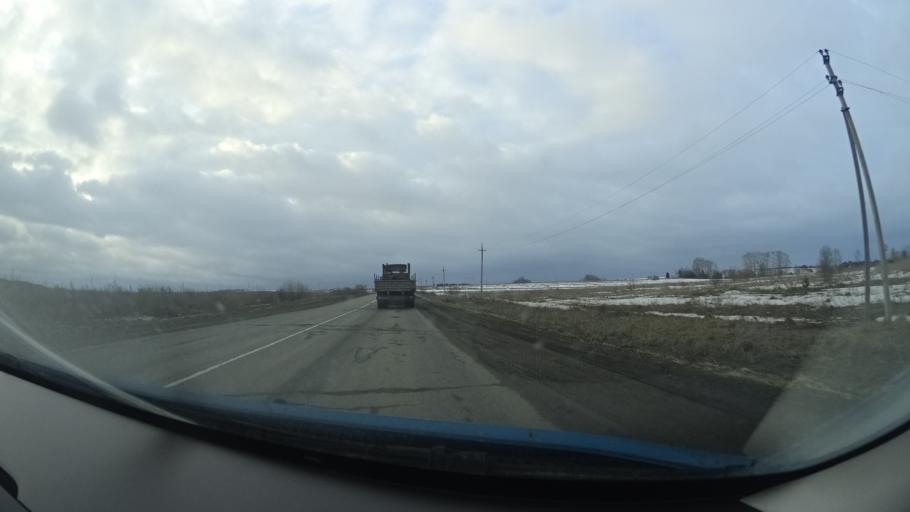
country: RU
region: Perm
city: Osa
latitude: 57.2543
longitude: 55.5808
